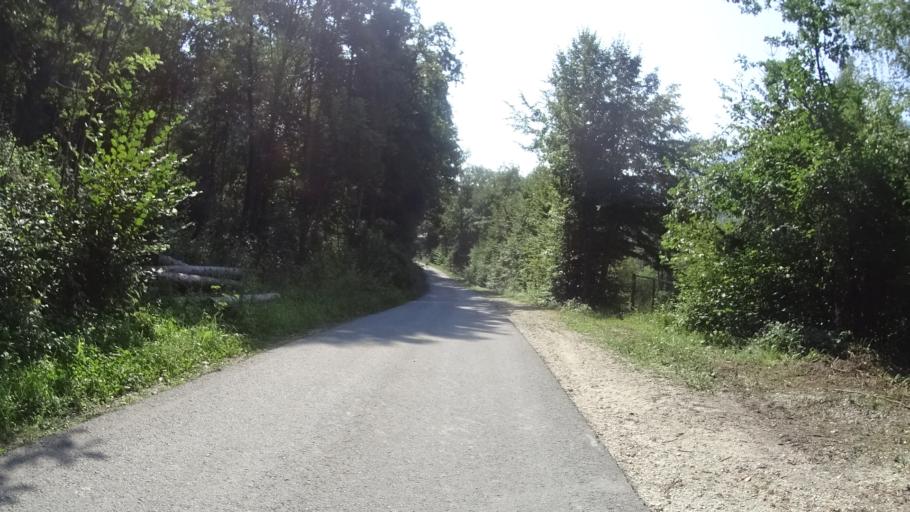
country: AT
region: Carinthia
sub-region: Politischer Bezirk Volkermarkt
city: Gallizien
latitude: 46.5694
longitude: 14.5267
